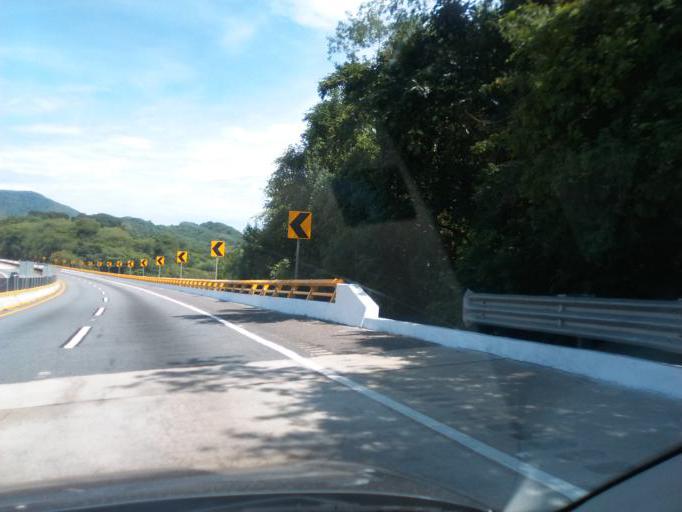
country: MX
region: Guerrero
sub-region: Acapulco de Juarez
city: Kilometro 30
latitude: 16.9873
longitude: -99.7021
